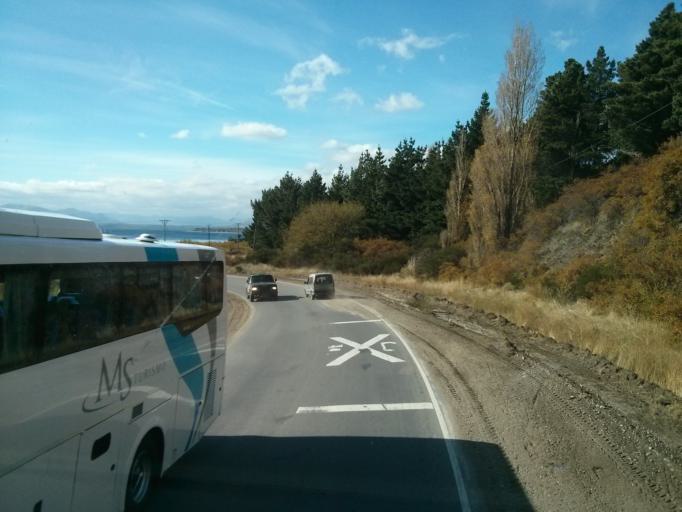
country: AR
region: Rio Negro
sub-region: Departamento de Bariloche
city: San Carlos de Bariloche
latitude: -41.1106
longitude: -71.2168
